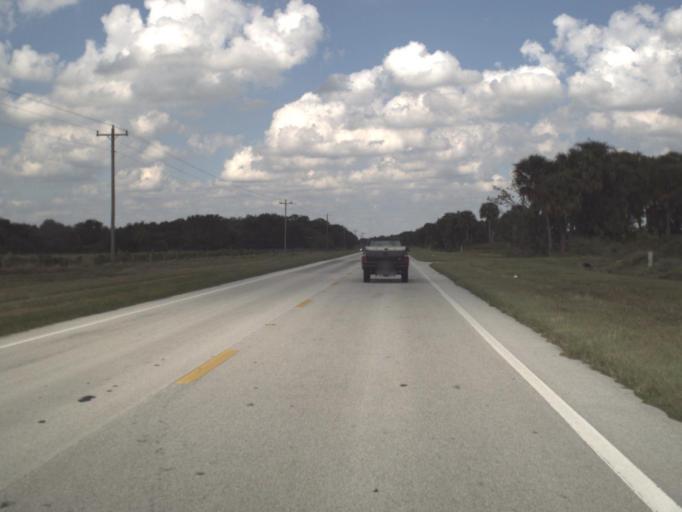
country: US
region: Florida
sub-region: Okeechobee County
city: Okeechobee
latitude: 27.3082
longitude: -80.9026
